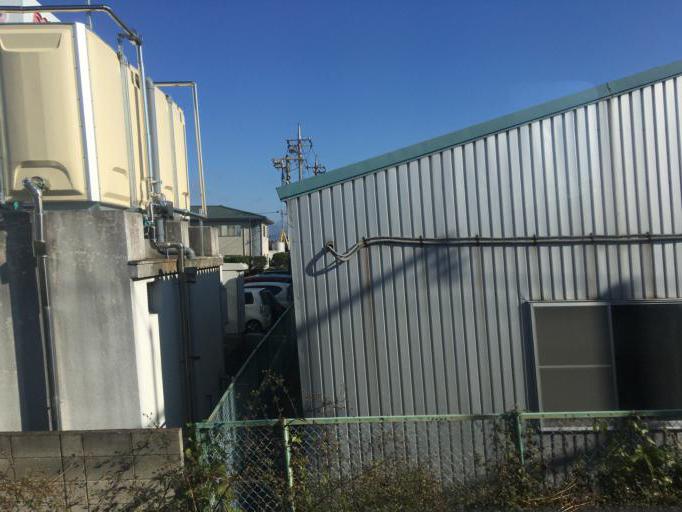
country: JP
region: Gunma
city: Maebashi-shi
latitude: 36.3688
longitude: 139.1128
